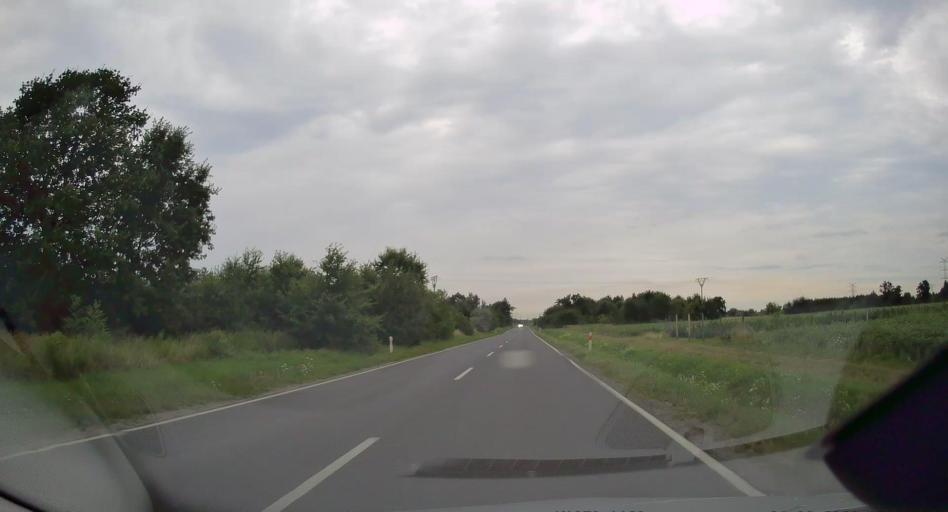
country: PL
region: Lesser Poland Voivodeship
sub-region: Powiat tarnowski
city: Wojnicz
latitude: 49.9695
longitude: 20.8460
